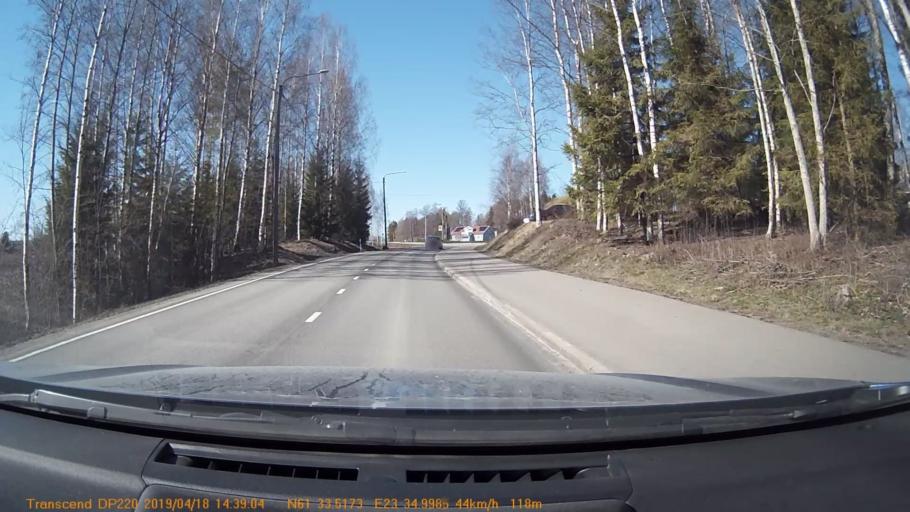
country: FI
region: Pirkanmaa
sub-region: Tampere
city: Yloejaervi
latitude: 61.5585
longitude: 23.5835
